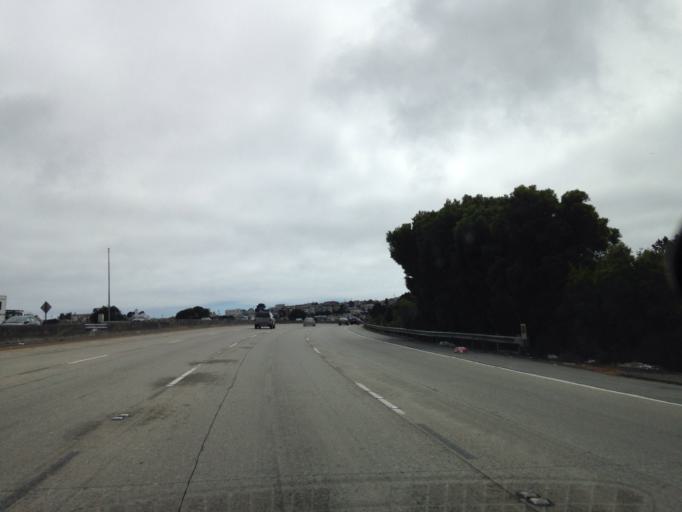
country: US
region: California
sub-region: San Mateo County
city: Daly City
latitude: 37.7119
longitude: -122.4542
